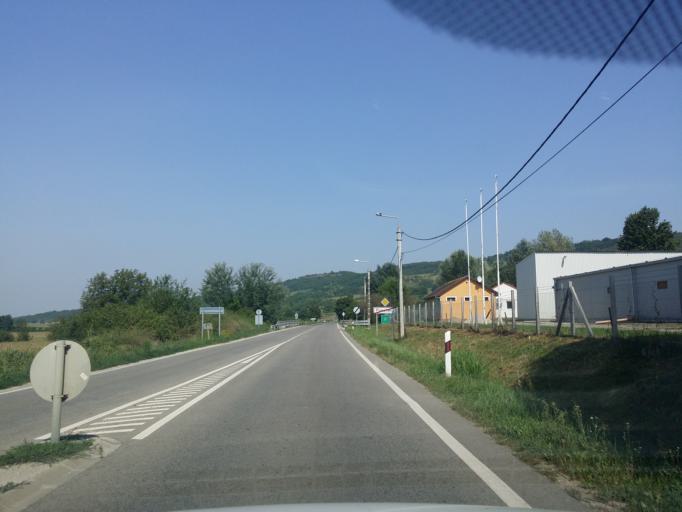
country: HU
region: Tolna
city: Pincehely
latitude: 46.6938
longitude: 18.4580
